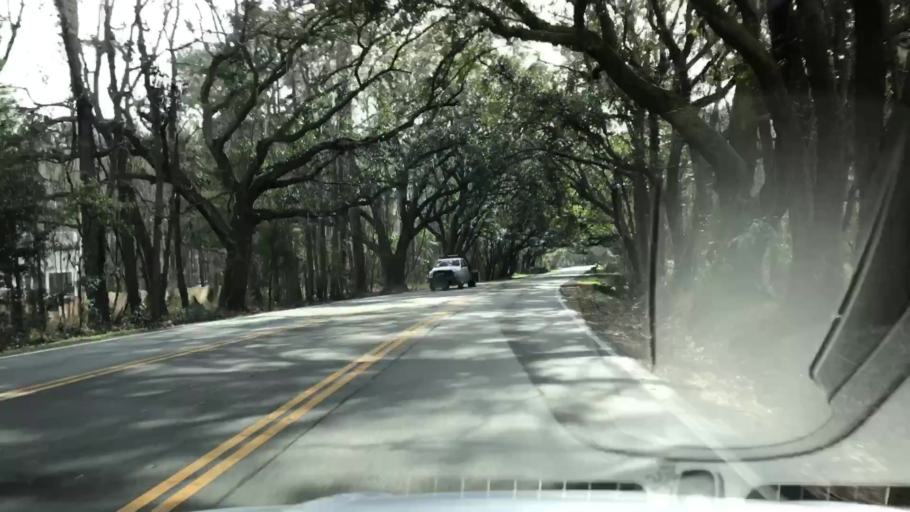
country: US
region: South Carolina
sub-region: Charleston County
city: Shell Point
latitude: 32.7286
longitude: -80.0258
